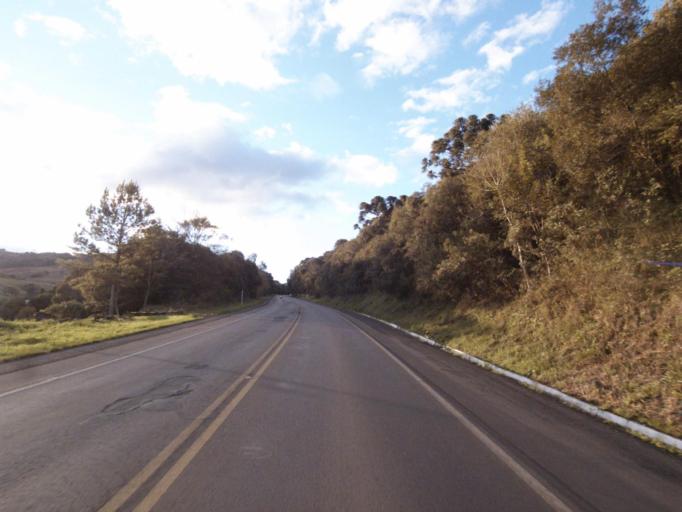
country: BR
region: Santa Catarina
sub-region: Joacaba
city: Joacaba
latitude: -27.2709
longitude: -51.4432
